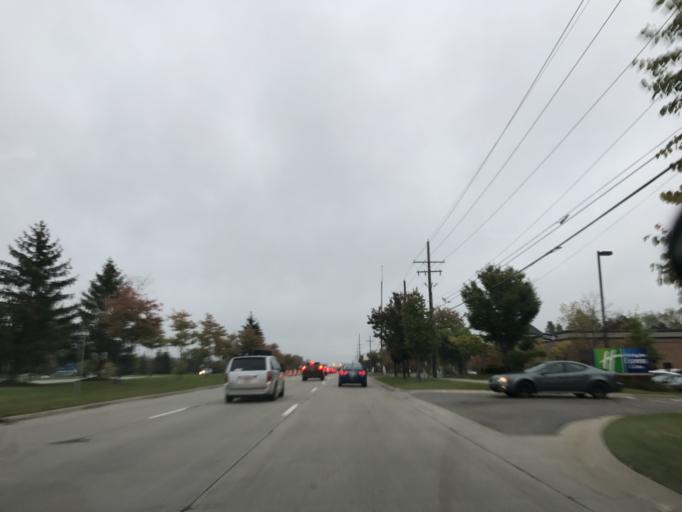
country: US
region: Michigan
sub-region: Oakland County
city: Novi
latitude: 42.4967
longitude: -83.4399
